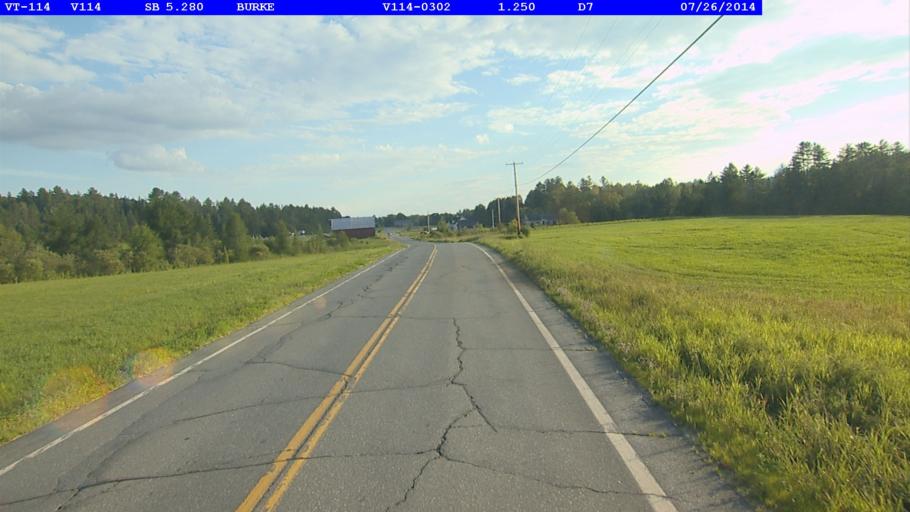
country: US
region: Vermont
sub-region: Caledonia County
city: Lyndonville
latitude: 44.5958
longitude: -71.9347
